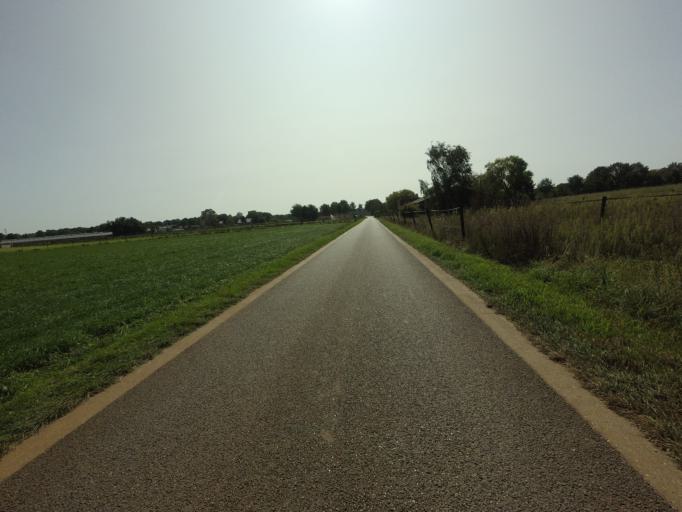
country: NL
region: Limburg
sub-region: Gemeente Roerdalen
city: Sint Odilienberg
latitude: 51.1428
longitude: 5.9837
